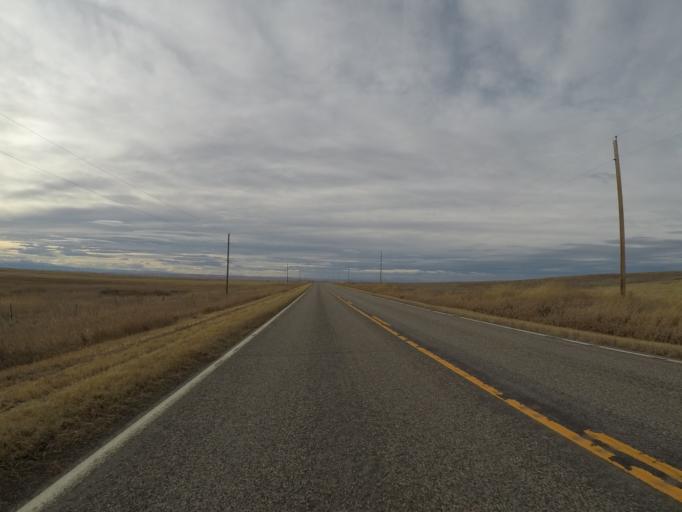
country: US
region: Montana
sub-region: Yellowstone County
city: Laurel
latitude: 45.8563
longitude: -108.7997
